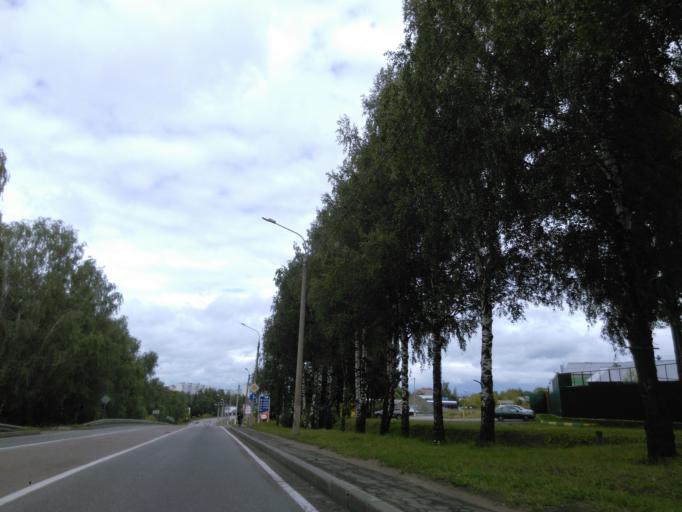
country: RU
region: Moskovskaya
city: Solnechnogorsk
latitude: 56.1834
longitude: 36.9606
